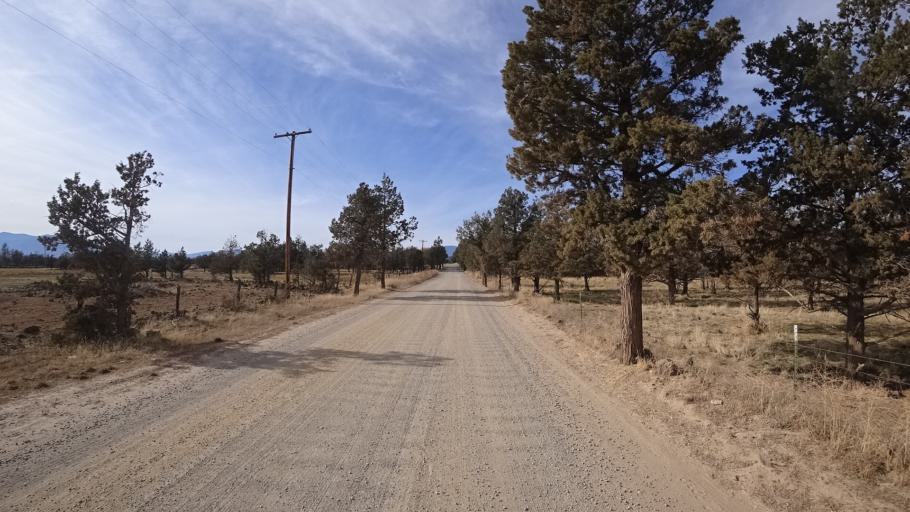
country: US
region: California
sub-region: Siskiyou County
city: Weed
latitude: 41.5954
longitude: -122.4063
